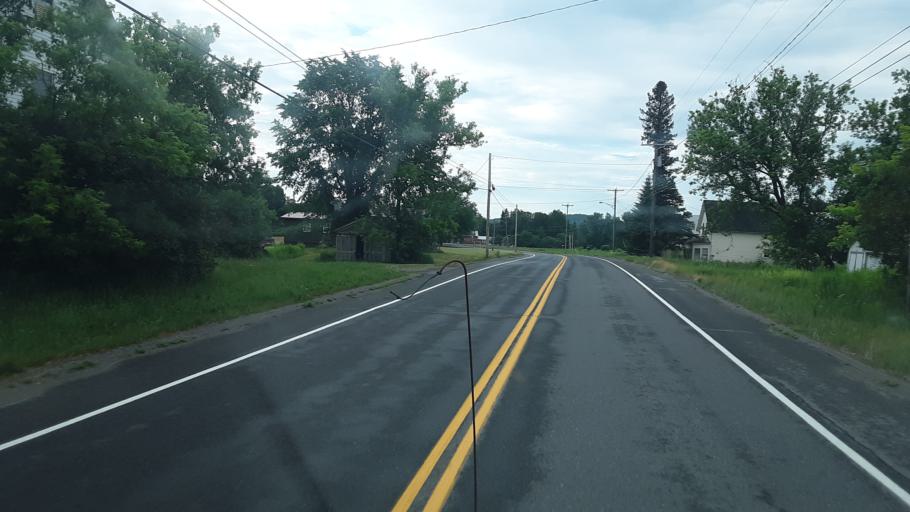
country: US
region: Maine
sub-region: Penobscot County
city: Patten
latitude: 45.9053
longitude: -68.4349
